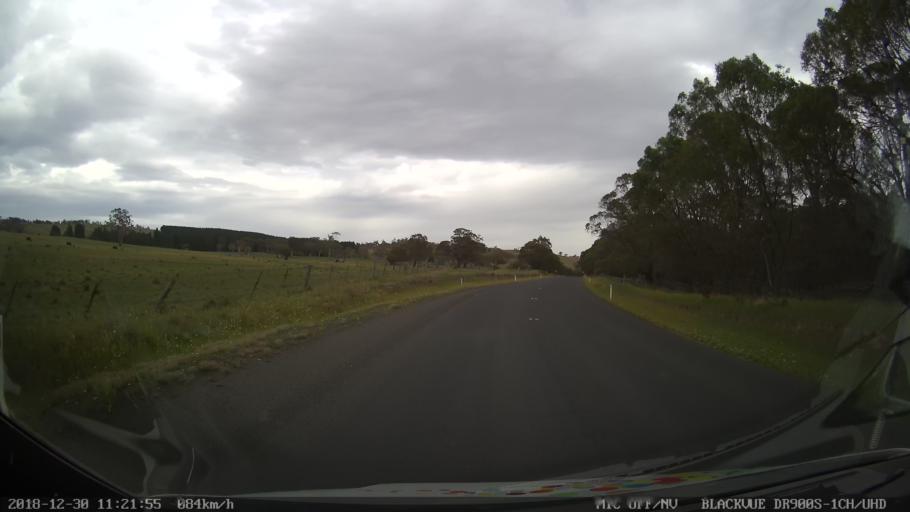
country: AU
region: New South Wales
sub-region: Snowy River
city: Jindabyne
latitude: -36.5061
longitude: 148.6725
